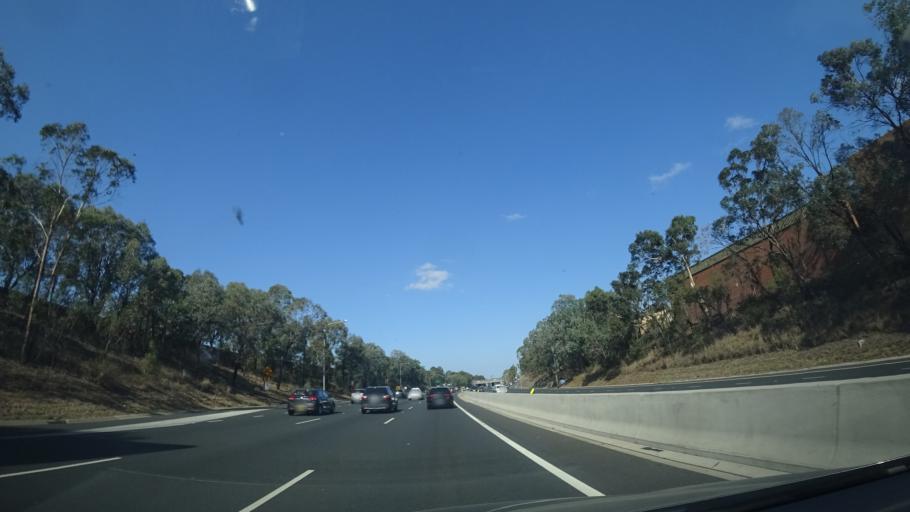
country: AU
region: New South Wales
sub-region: Bankstown
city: Revesby
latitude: -33.9400
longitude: 151.0302
